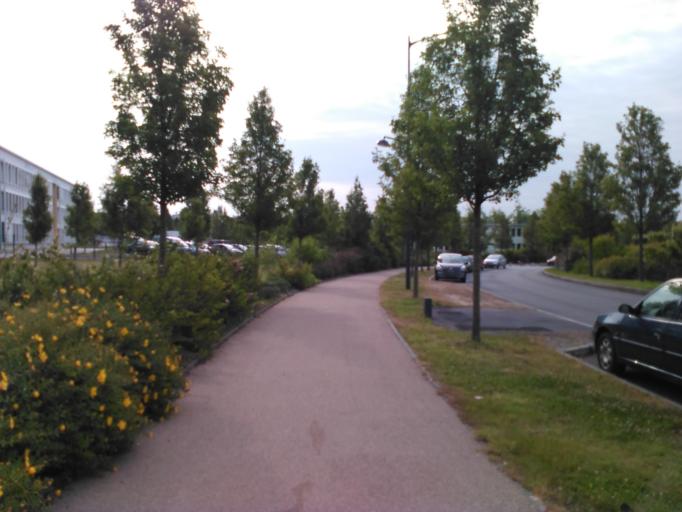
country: FR
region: Brittany
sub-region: Departement d'Ille-et-Vilaine
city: Rennes
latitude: 48.1149
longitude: -1.7132
